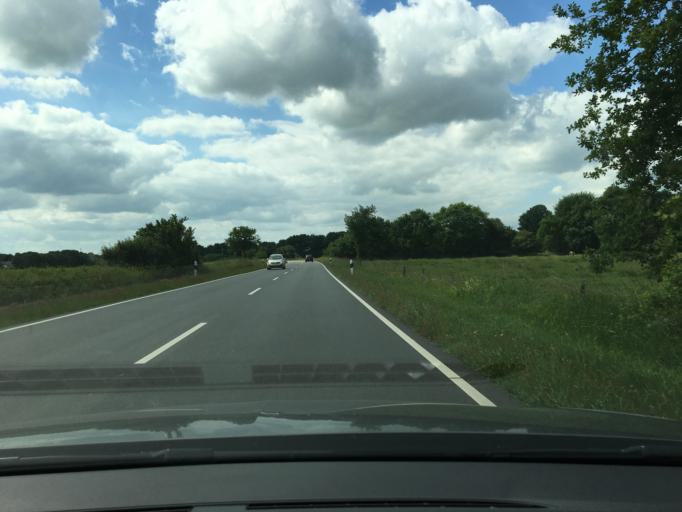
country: DE
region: Schleswig-Holstein
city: Kropp
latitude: 54.4222
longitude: 9.4941
